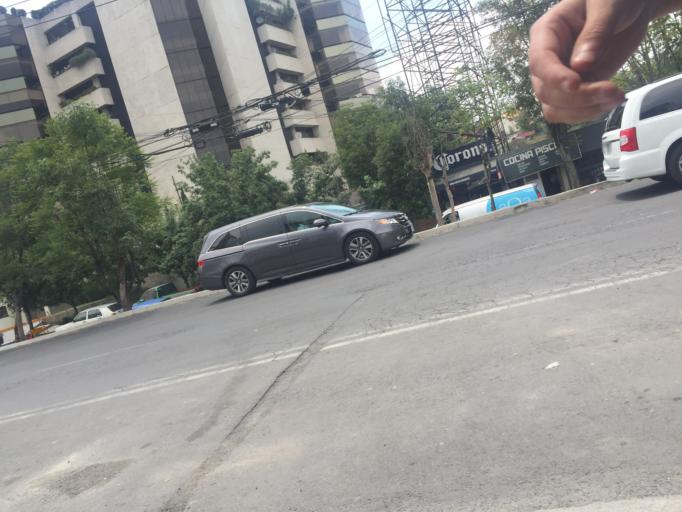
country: MX
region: Mexico City
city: Col. Bosques de las Lomas
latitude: 19.3889
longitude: -99.2622
